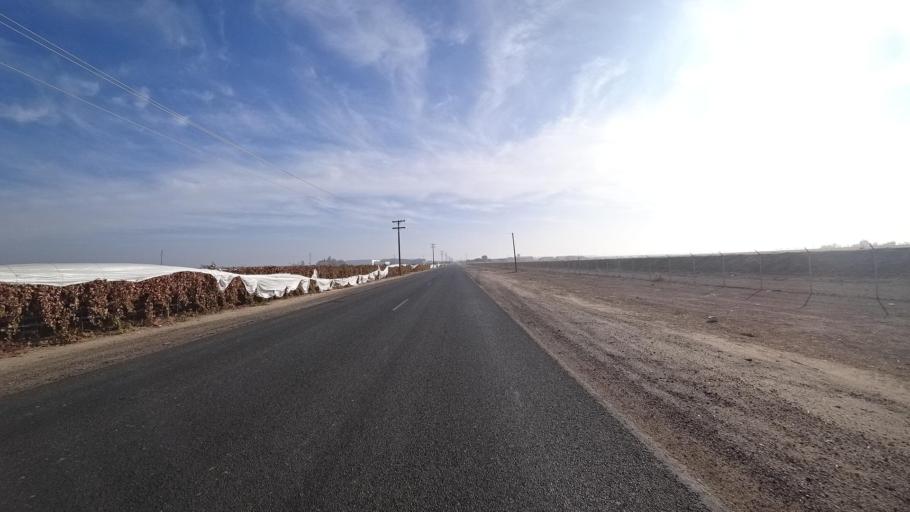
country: US
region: California
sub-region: Kern County
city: McFarland
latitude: 35.6021
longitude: -119.2018
